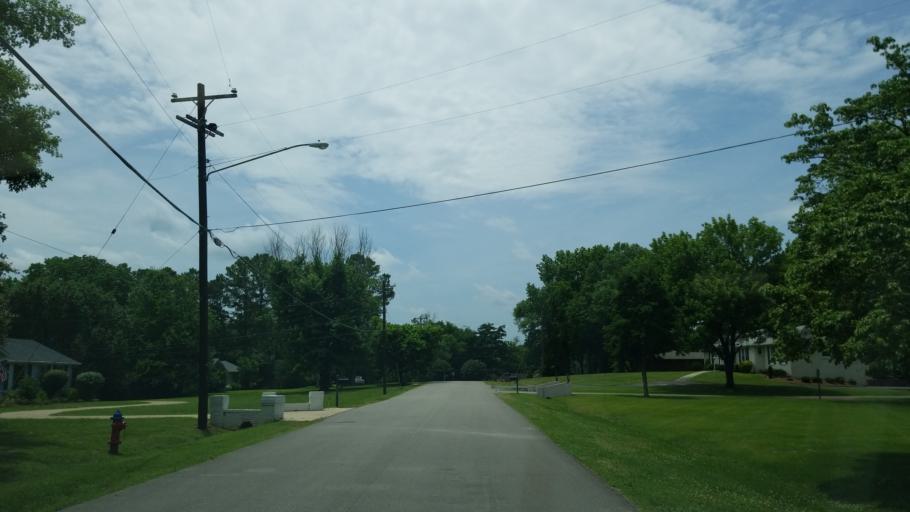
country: US
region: Tennessee
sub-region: Williamson County
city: Brentwood
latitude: 36.0311
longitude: -86.7948
